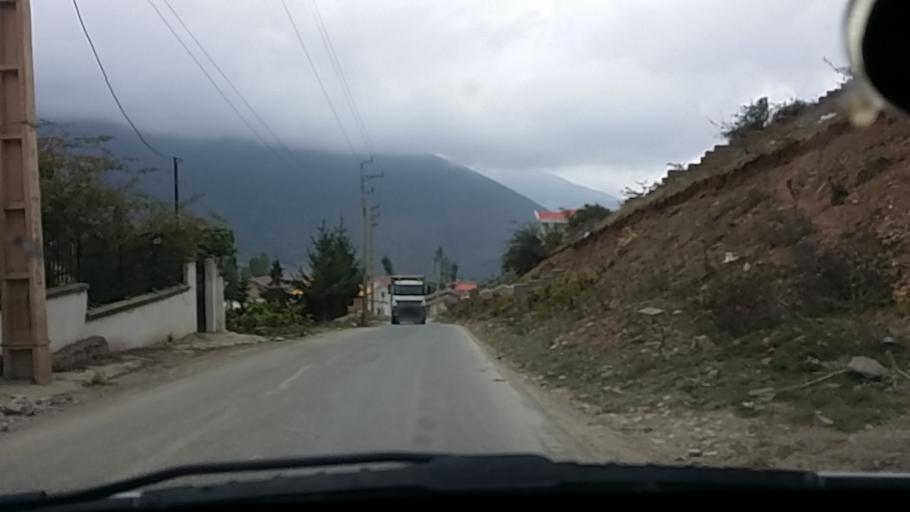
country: IR
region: Mazandaran
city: `Abbasabad
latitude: 36.4766
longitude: 51.1399
